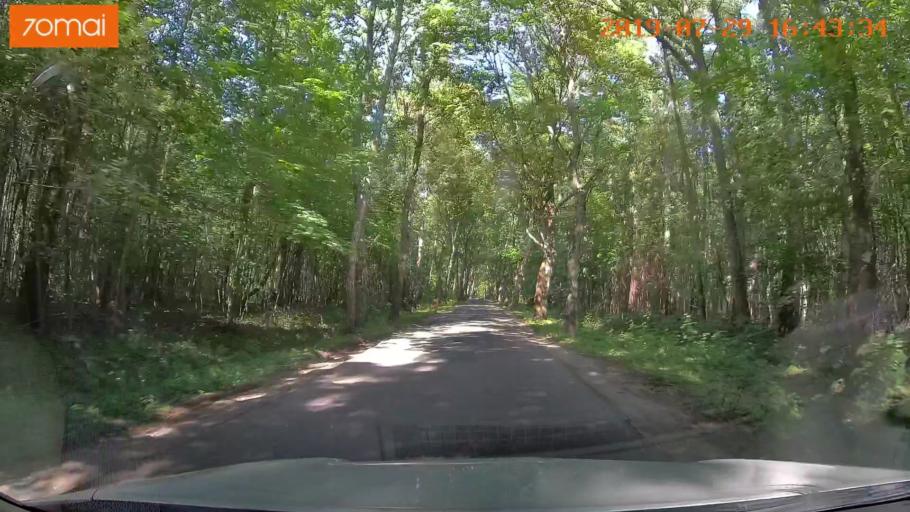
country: RU
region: Kaliningrad
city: Primorsk
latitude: 54.7497
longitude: 20.0857
